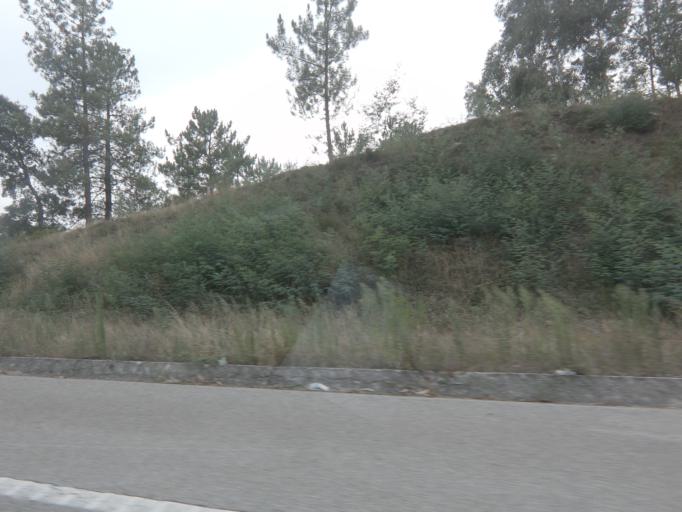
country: PT
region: Coimbra
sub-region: Penacova
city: Lorvao
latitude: 40.2948
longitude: -8.3089
